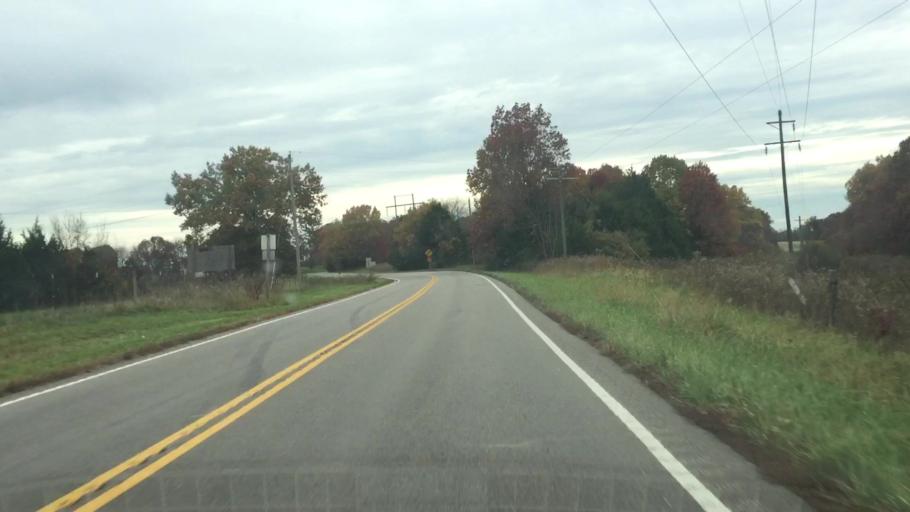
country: US
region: Missouri
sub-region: Gasconade County
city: Hermann
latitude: 38.7229
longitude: -91.7060
